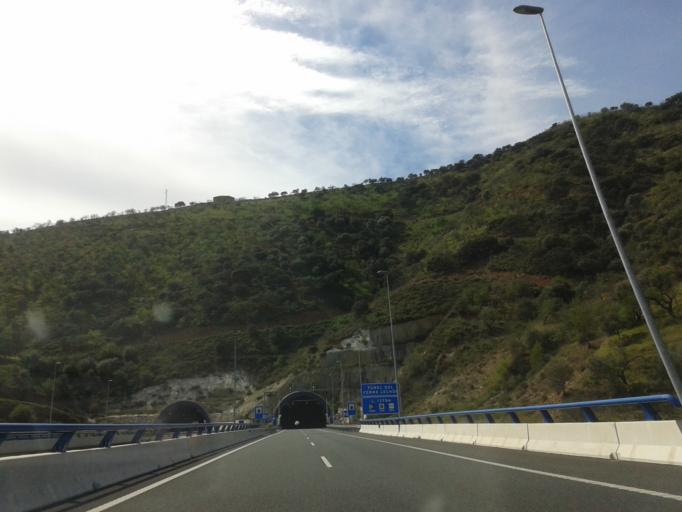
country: ES
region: Andalusia
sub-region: Provincia de Malaga
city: Casabermeja
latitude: 36.8716
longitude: -4.4834
